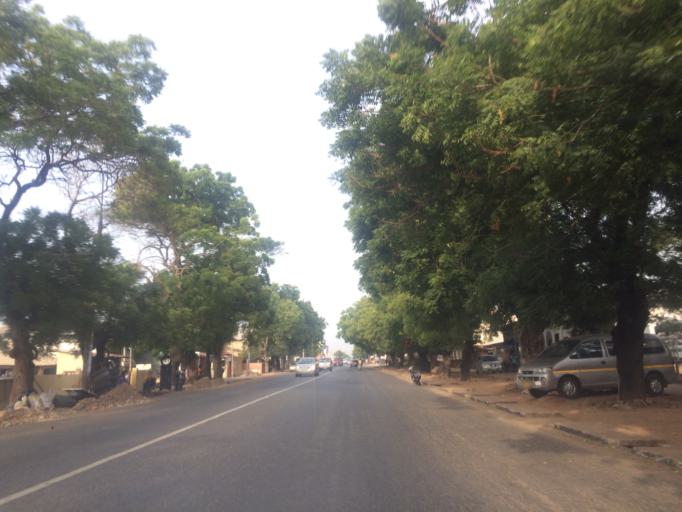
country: GH
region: Greater Accra
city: Accra
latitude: 5.5366
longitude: -0.2247
